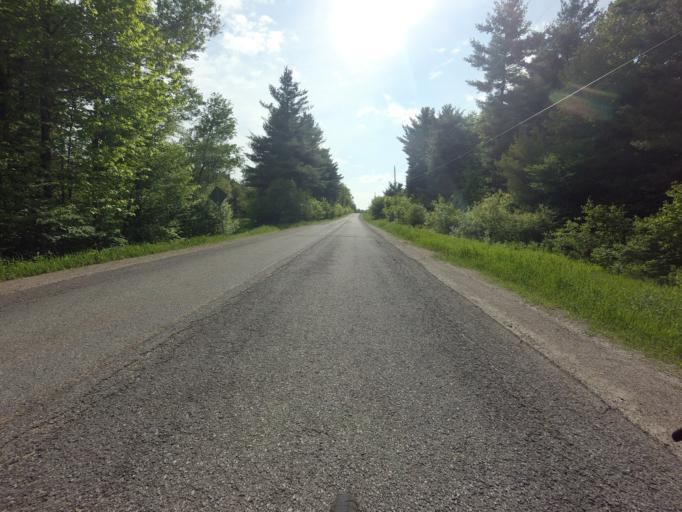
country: US
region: New York
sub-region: St. Lawrence County
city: Gouverneur
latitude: 44.2613
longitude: -75.2146
